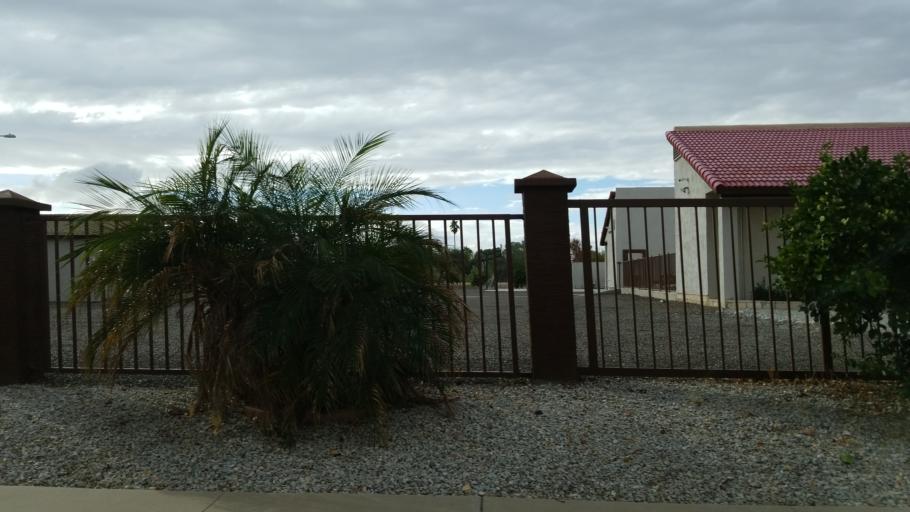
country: US
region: Arizona
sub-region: Maricopa County
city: Glendale
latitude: 33.6079
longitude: -112.1079
